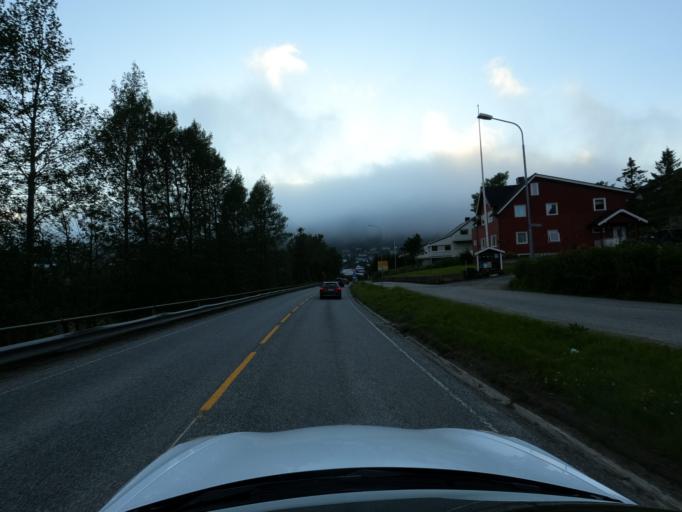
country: NO
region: Troms
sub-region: Harstad
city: Harstad
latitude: 68.8061
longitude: 16.5129
